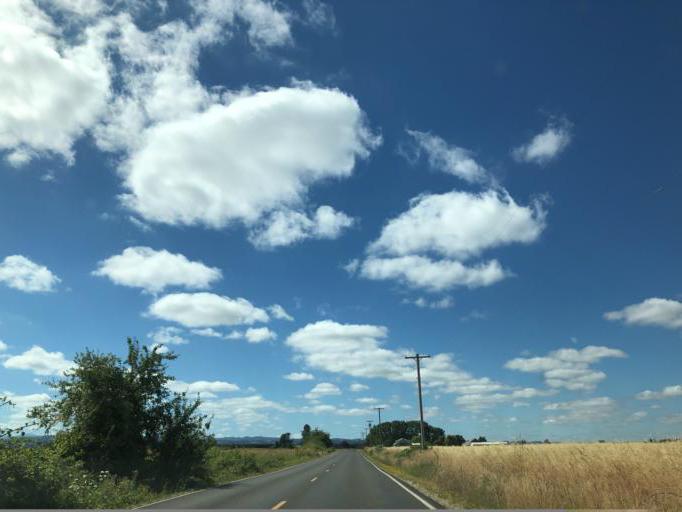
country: US
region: Oregon
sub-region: Marion County
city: Mount Angel
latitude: 45.1170
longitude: -122.7287
